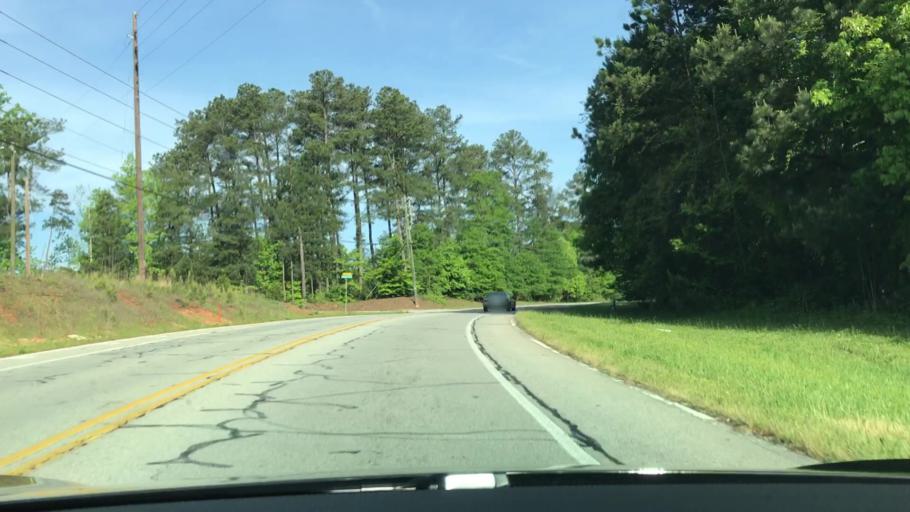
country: US
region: Georgia
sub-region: Gwinnett County
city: Sugar Hill
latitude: 34.1452
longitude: -84.0592
